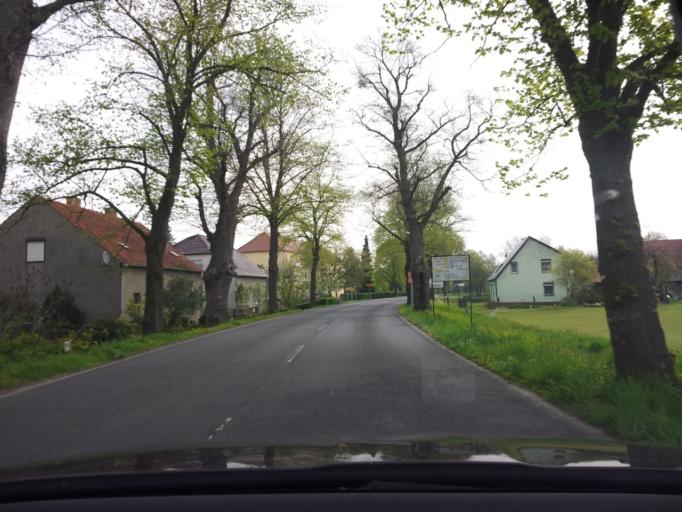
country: DE
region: Brandenburg
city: Drahnsdorf
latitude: 51.8536
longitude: 13.6027
